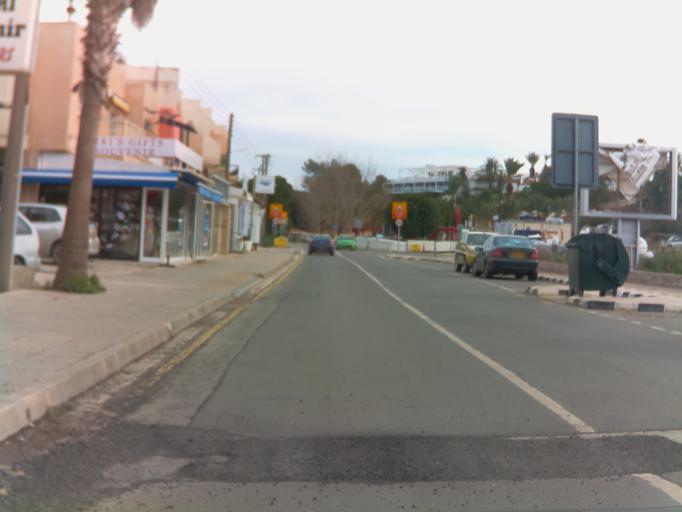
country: CY
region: Pafos
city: Polis
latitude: 35.0403
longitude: 32.3956
